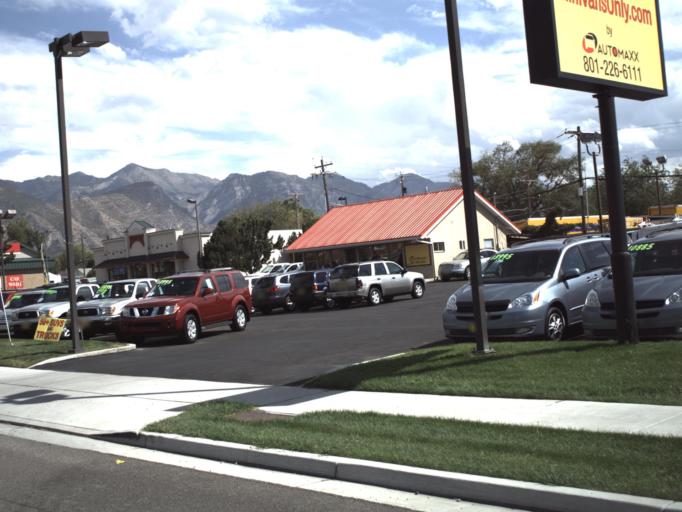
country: US
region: Utah
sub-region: Utah County
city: Orem
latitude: 40.3118
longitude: -111.7019
